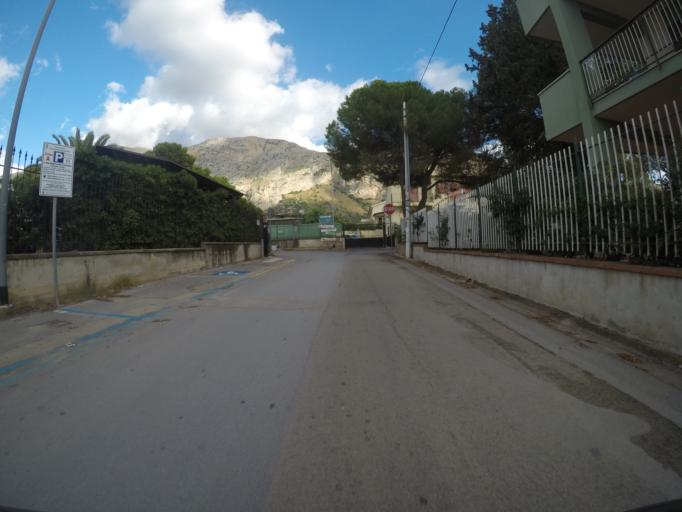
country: IT
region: Sicily
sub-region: Palermo
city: Isola delle Femmine
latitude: 38.1852
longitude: 13.2409
